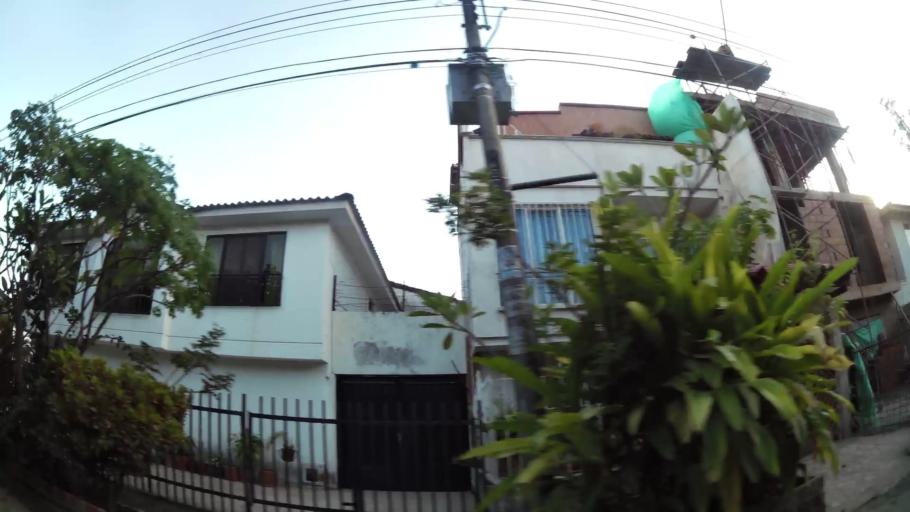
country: CO
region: Valle del Cauca
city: Cali
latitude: 3.4060
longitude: -76.5539
